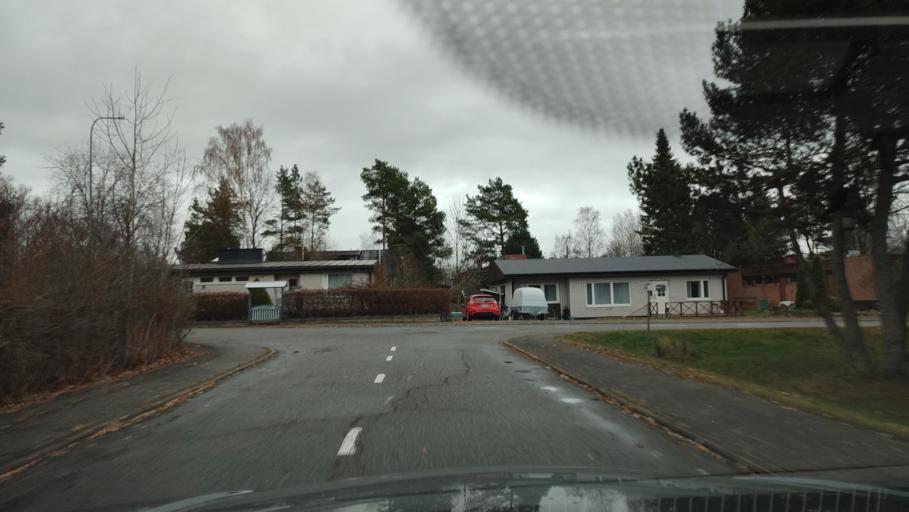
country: FI
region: Ostrobothnia
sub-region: Sydosterbotten
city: Kristinestad
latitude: 62.2811
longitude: 21.3725
